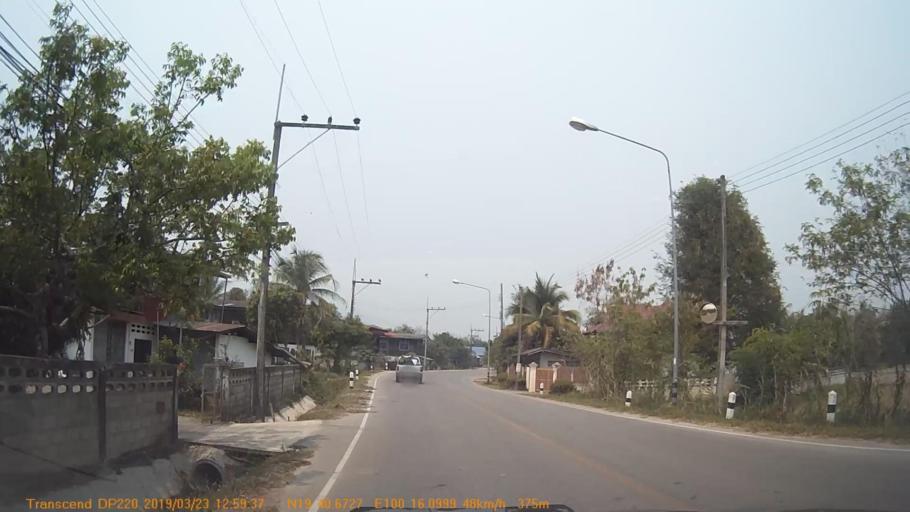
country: TH
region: Chiang Rai
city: Thoeng
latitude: 19.6781
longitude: 100.2684
